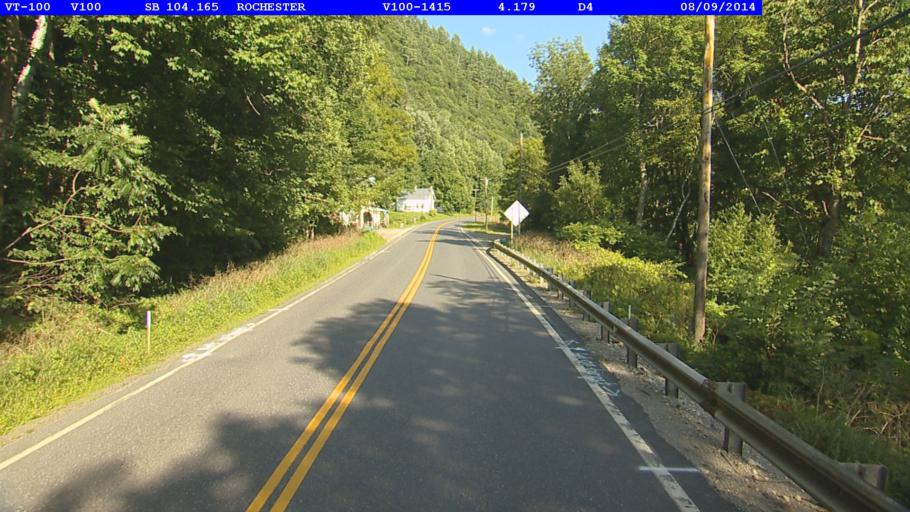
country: US
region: Vermont
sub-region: Orange County
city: Randolph
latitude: 43.8597
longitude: -72.8084
